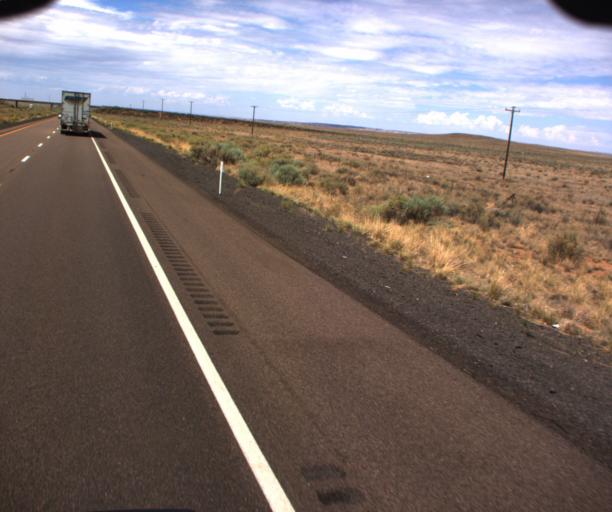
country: US
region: Arizona
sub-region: Navajo County
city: Holbrook
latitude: 35.0507
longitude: -109.7986
